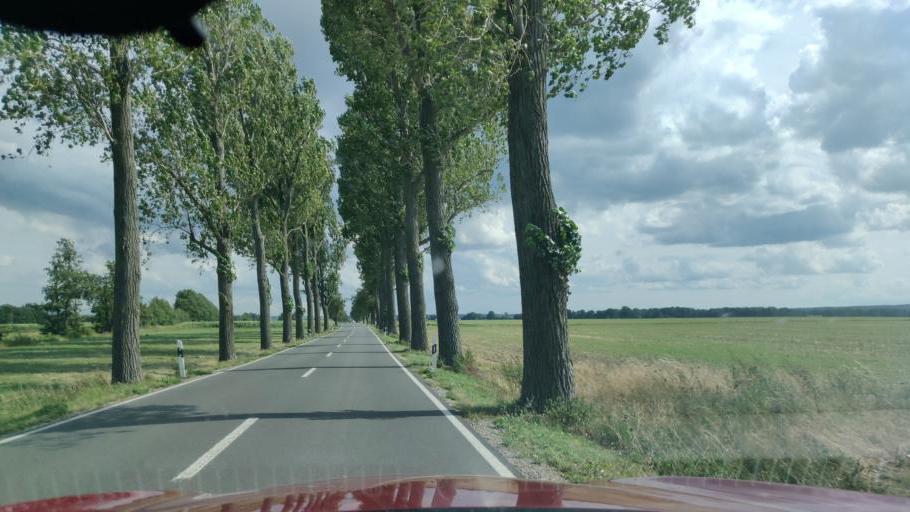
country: DE
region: Saxony
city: Schildau
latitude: 51.4881
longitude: 12.9173
